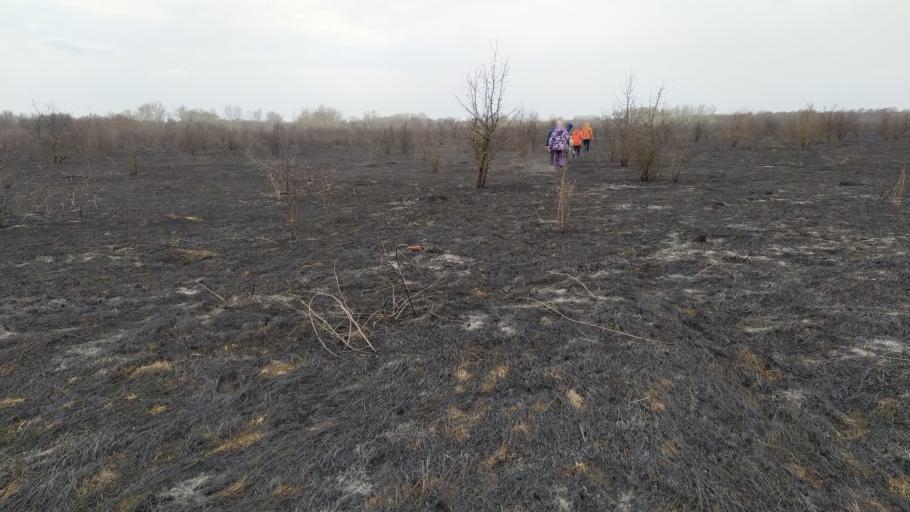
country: RU
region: Rostov
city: Semikarakorsk
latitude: 47.5447
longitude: 40.6843
